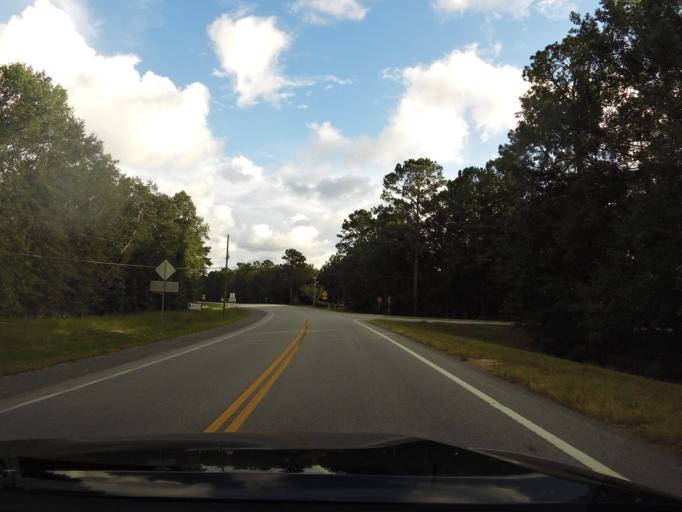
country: US
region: Georgia
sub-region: Liberty County
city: Midway
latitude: 31.7679
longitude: -81.4493
